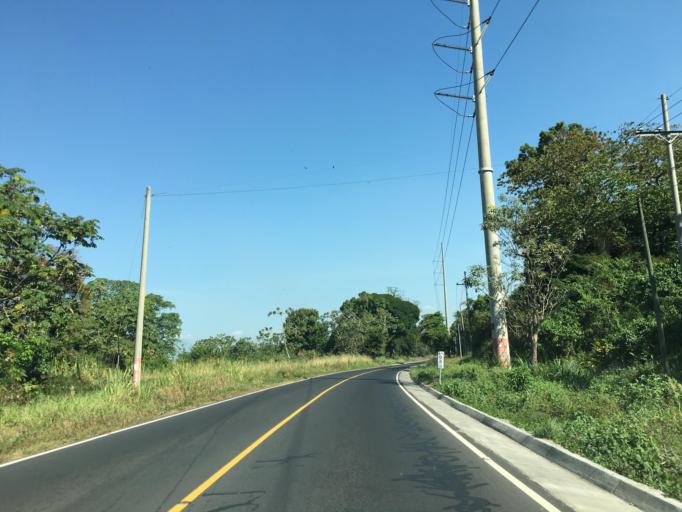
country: GT
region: Escuintla
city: Siquinala
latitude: 14.2824
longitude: -90.9686
